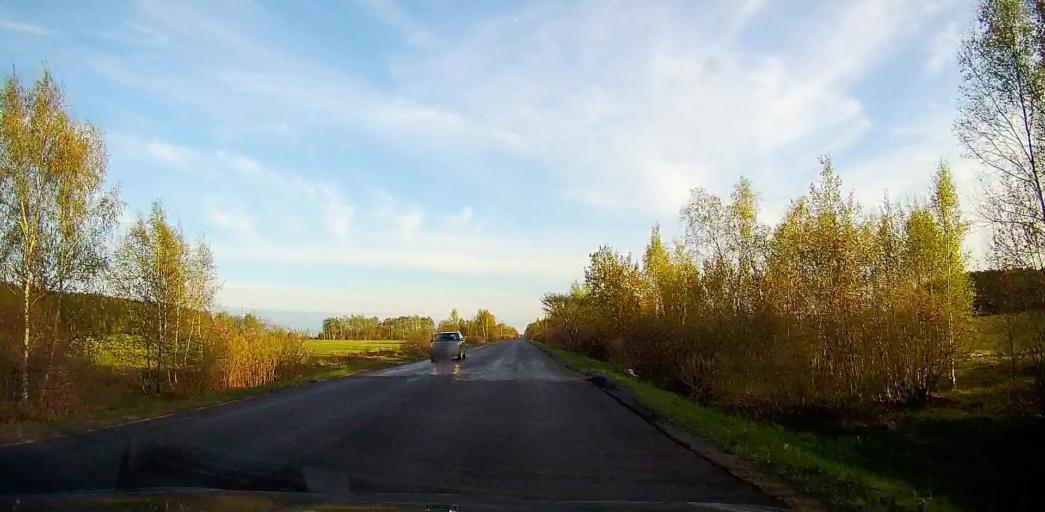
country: RU
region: Moskovskaya
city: Bronnitsy
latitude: 55.2828
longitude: 38.2172
